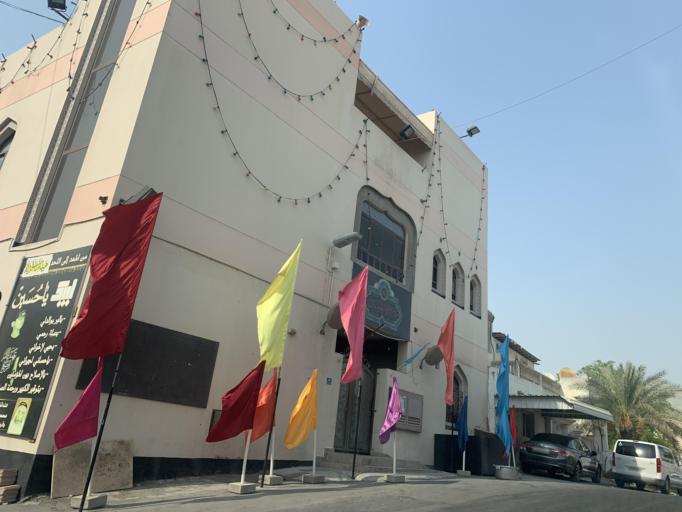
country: BH
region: Manama
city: Jidd Hafs
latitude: 26.2209
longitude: 50.4872
